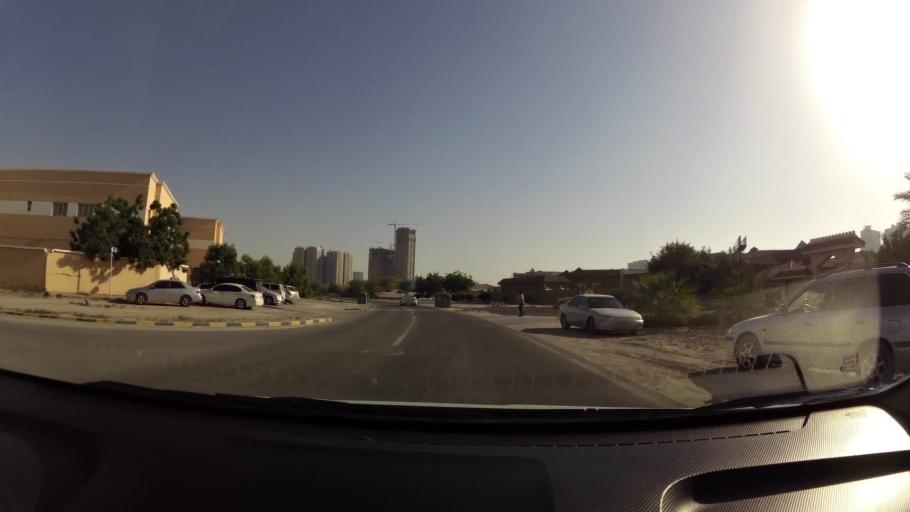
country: AE
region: Ajman
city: Ajman
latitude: 25.4037
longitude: 55.4586
